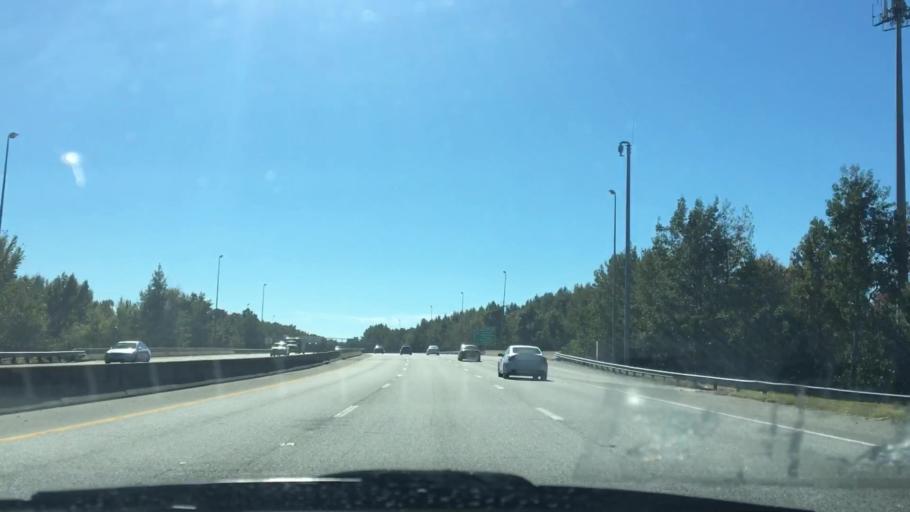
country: US
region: Virginia
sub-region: City of Portsmouth
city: Portsmouth Heights
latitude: 36.8161
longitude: -76.3472
